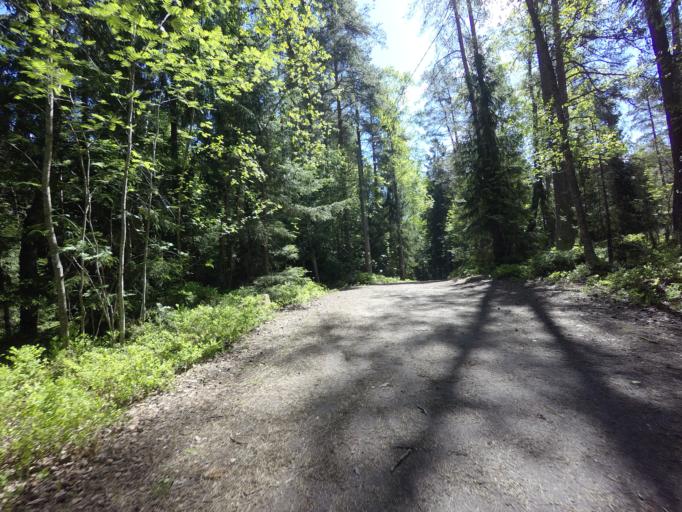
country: FI
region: Uusimaa
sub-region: Helsinki
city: Kauniainen
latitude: 60.1801
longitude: 24.7284
